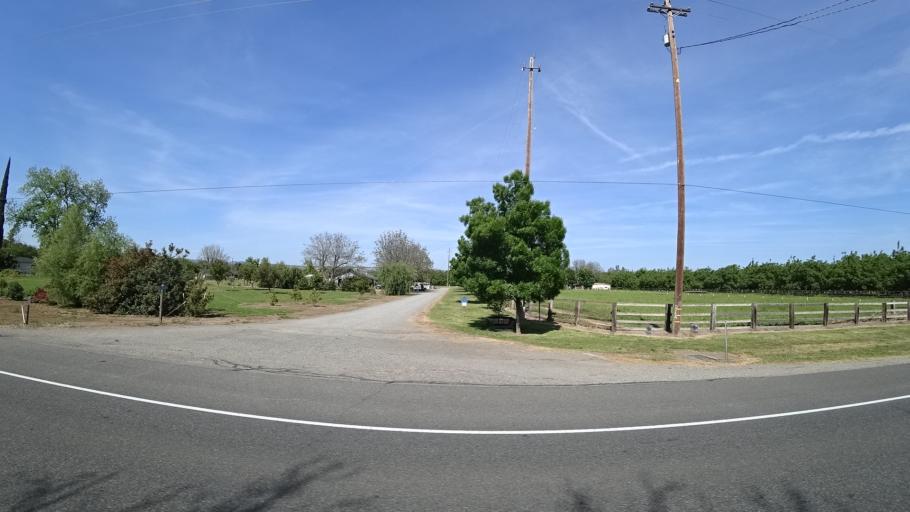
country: US
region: California
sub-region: Tehama County
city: Red Bluff
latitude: 40.1527
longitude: -122.1427
